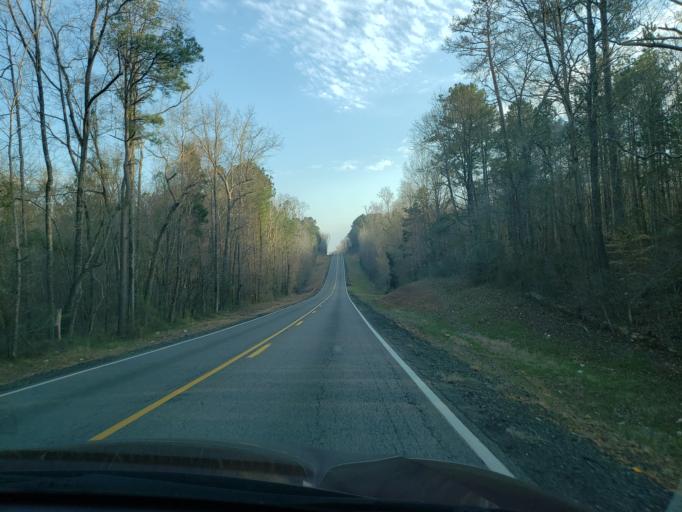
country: US
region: Alabama
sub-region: Hale County
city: Greensboro
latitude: 32.7892
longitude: -87.5901
